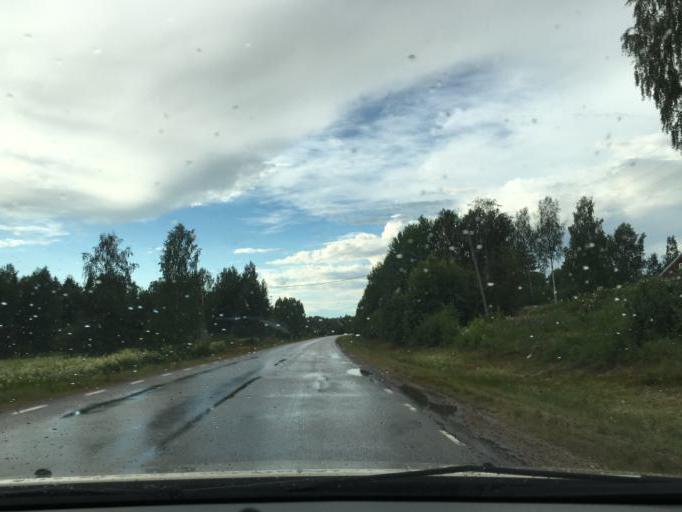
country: SE
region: Norrbotten
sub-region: Kalix Kommun
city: Toere
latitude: 66.0060
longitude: 22.8509
